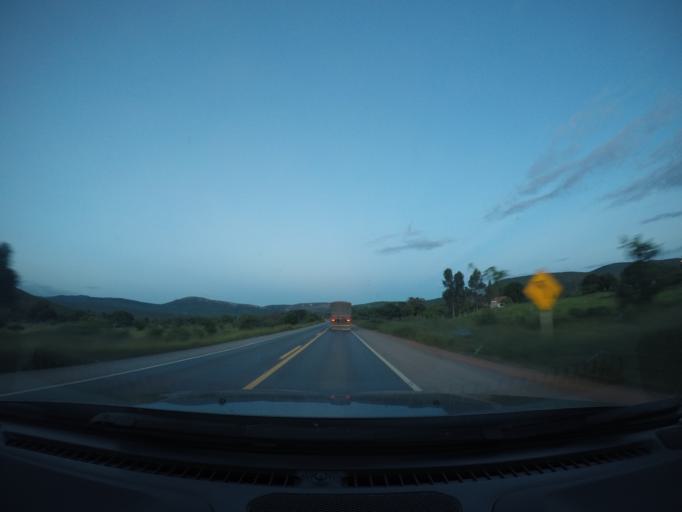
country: BR
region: Bahia
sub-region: Seabra
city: Seabra
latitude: -12.4857
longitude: -41.7245
